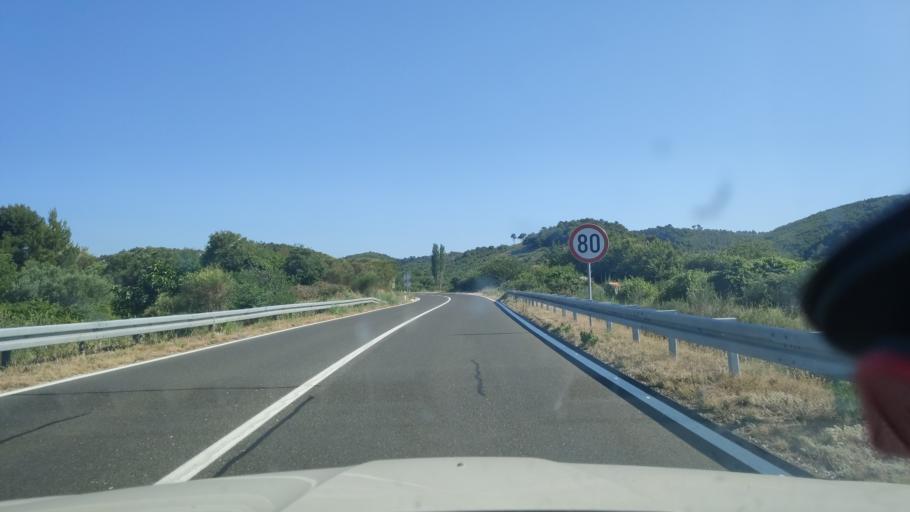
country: HR
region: Sibensko-Kniniska
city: Zaton
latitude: 43.8442
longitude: 15.8983
